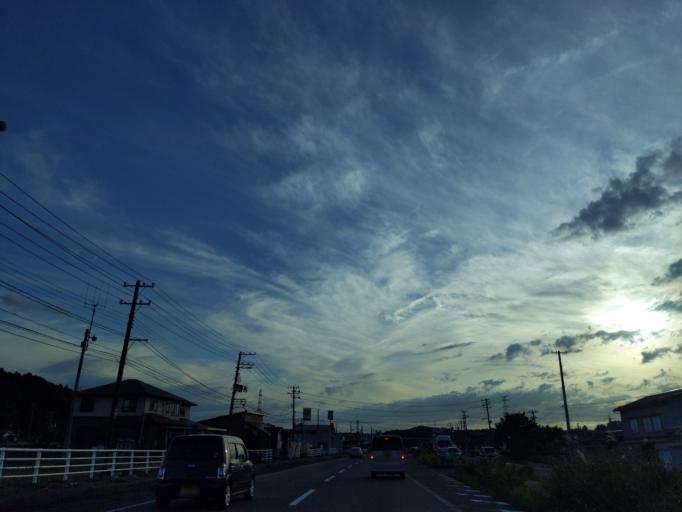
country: JP
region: Niigata
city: Kashiwazaki
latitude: 37.4482
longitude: 138.6427
